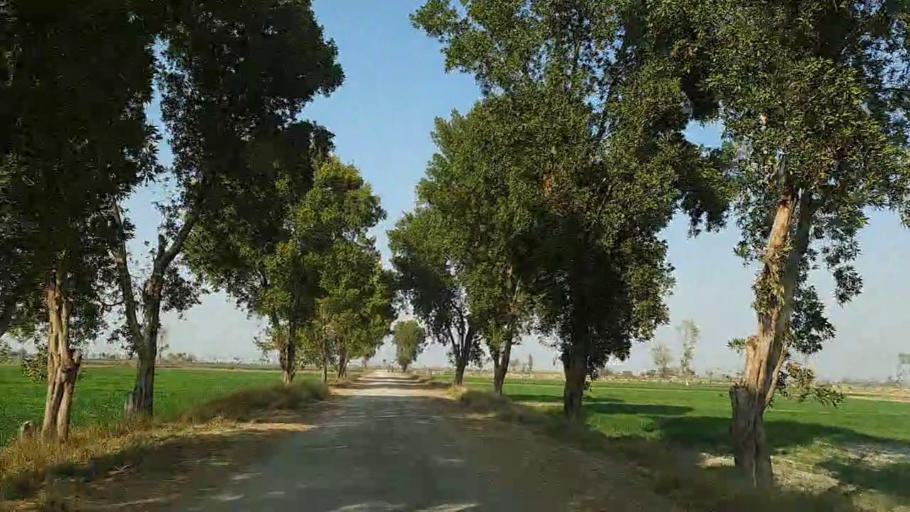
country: PK
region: Sindh
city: Daur
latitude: 26.4853
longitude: 68.2973
